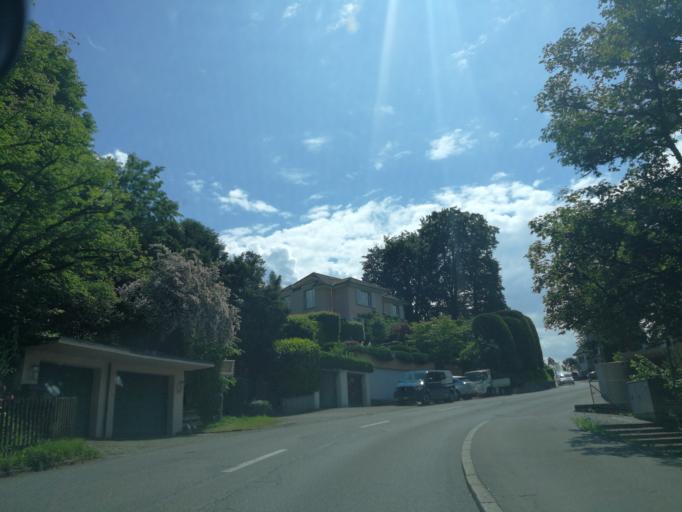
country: CH
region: Zurich
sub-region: Bezirk Meilen
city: Kuesnacht / Schiedhalden
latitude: 47.3209
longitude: 8.5879
